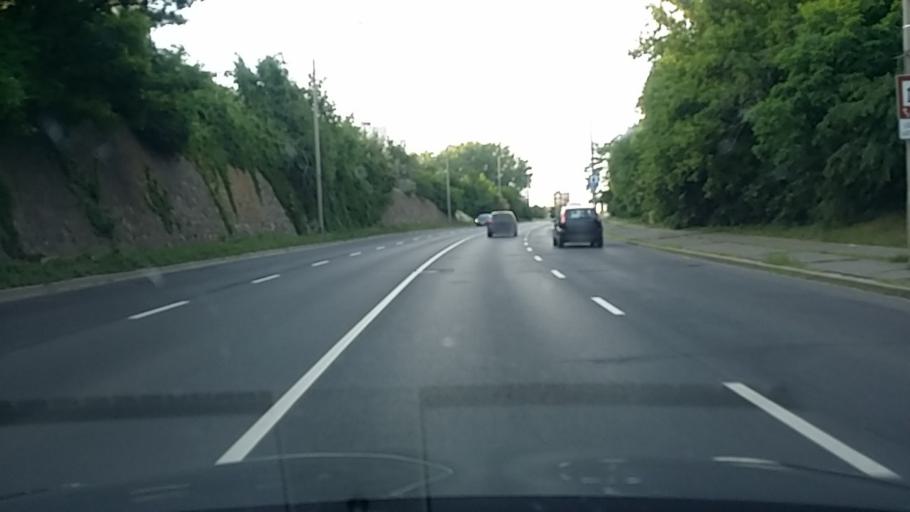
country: HU
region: Borsod-Abauj-Zemplen
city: Miskolc
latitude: 48.0788
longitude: 20.7843
